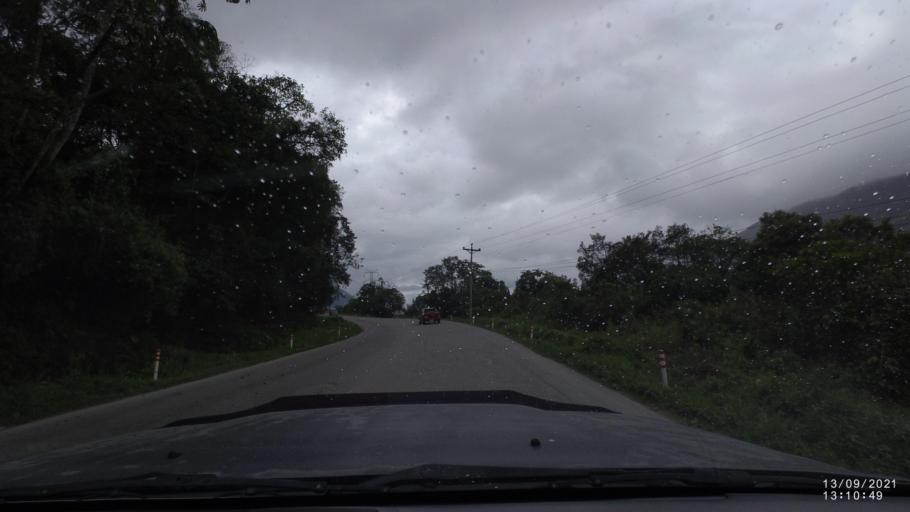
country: BO
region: Cochabamba
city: Colomi
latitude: -17.2057
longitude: -65.8295
